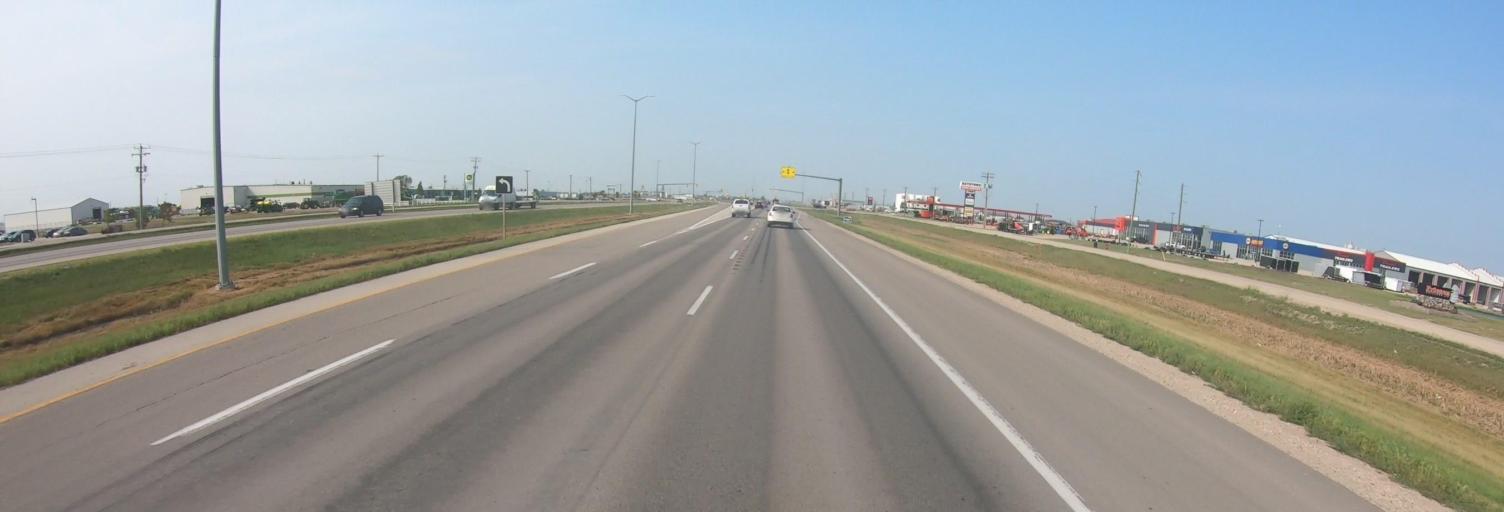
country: CA
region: Manitoba
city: Steinbach
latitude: 49.5574
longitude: -96.6875
